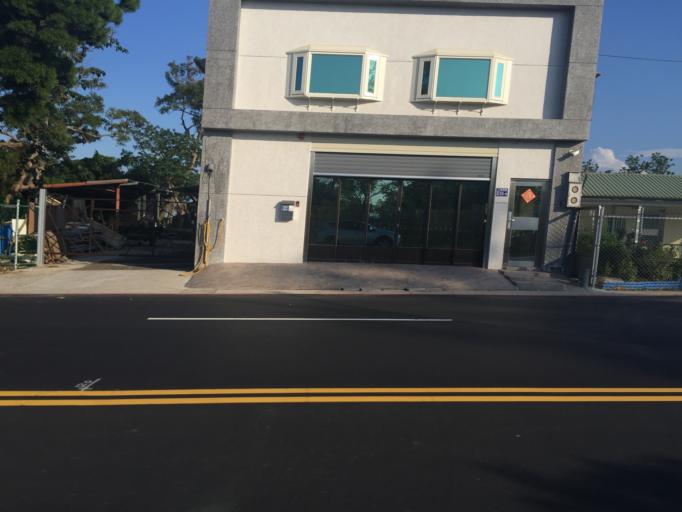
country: TW
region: Taiwan
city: Taoyuan City
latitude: 24.9432
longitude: 121.2648
